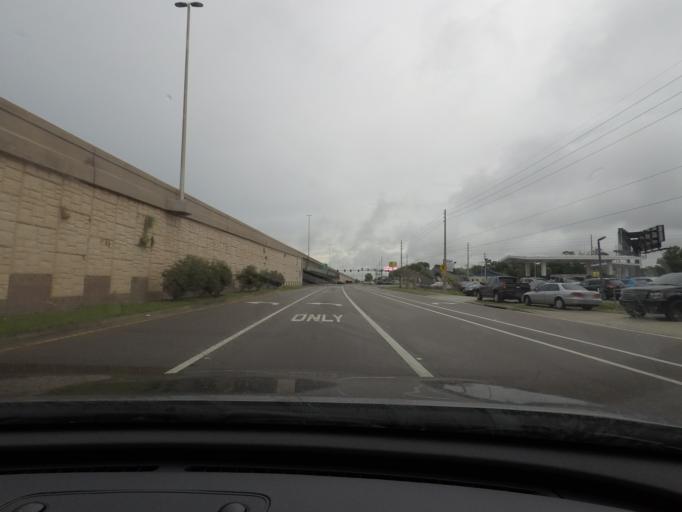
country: US
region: Florida
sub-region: Orange County
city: Azalea Park
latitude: 28.5582
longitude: -81.3097
